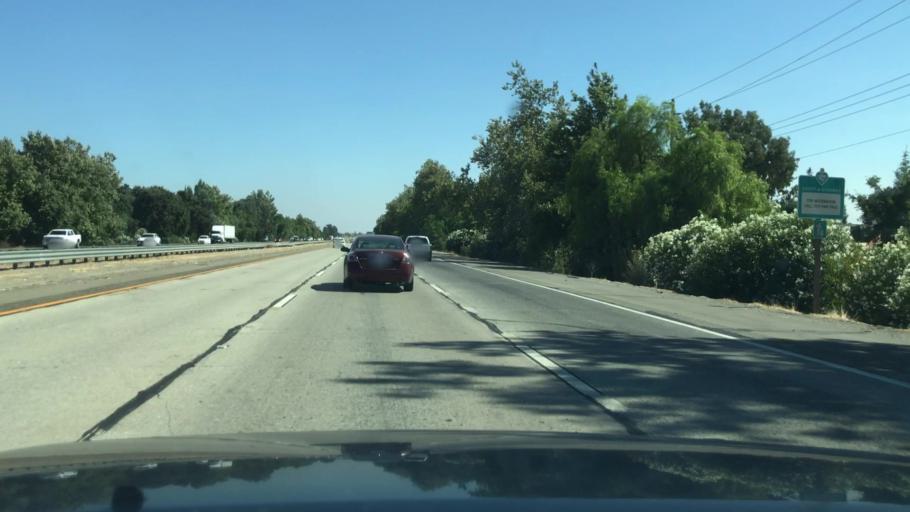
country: US
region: California
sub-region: San Joaquin County
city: Lincoln Village
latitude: 38.0313
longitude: -121.3640
